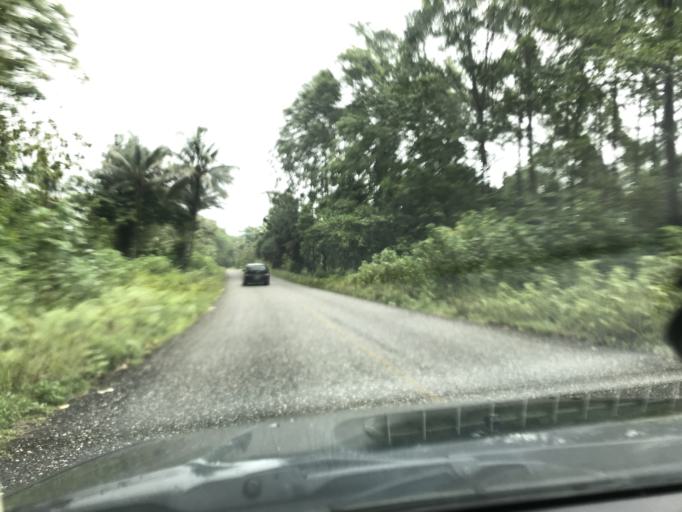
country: SB
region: Western Province
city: Gizo
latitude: -8.2367
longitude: 157.2215
